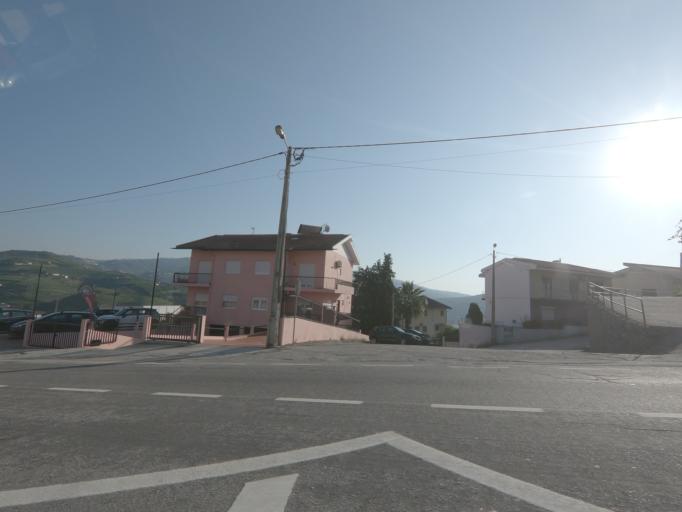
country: PT
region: Vila Real
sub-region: Peso da Regua
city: Peso da Regua
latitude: 41.1623
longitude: -7.7804
